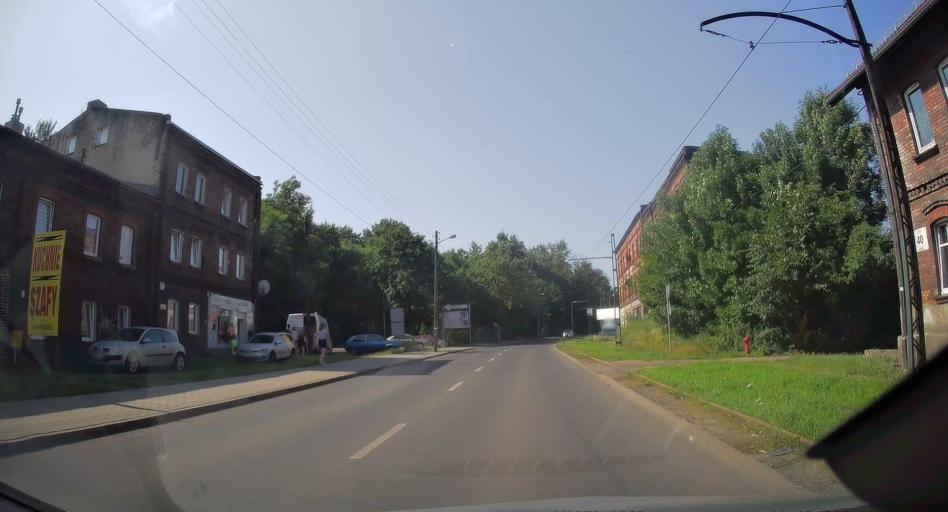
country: PL
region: Silesian Voivodeship
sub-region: Swietochlowice
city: Swietochlowice
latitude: 50.2792
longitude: 18.9119
